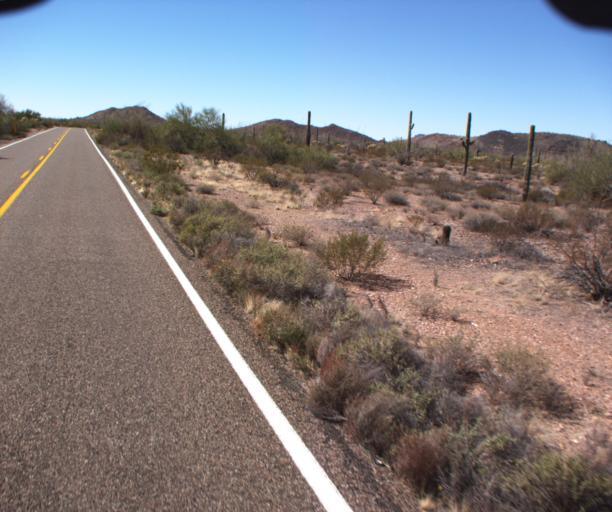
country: MX
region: Sonora
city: Sonoyta
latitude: 32.1037
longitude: -112.7708
